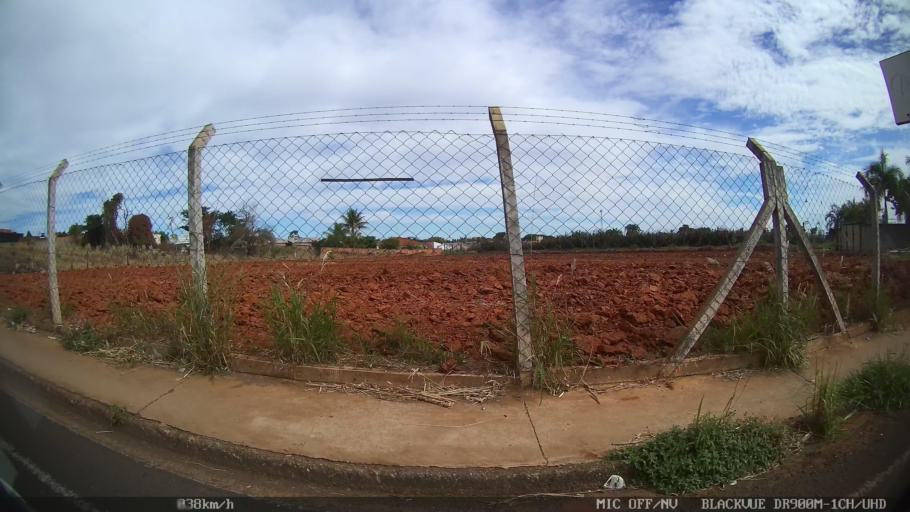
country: BR
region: Sao Paulo
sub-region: Catanduva
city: Catanduva
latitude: -21.1556
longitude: -48.9633
